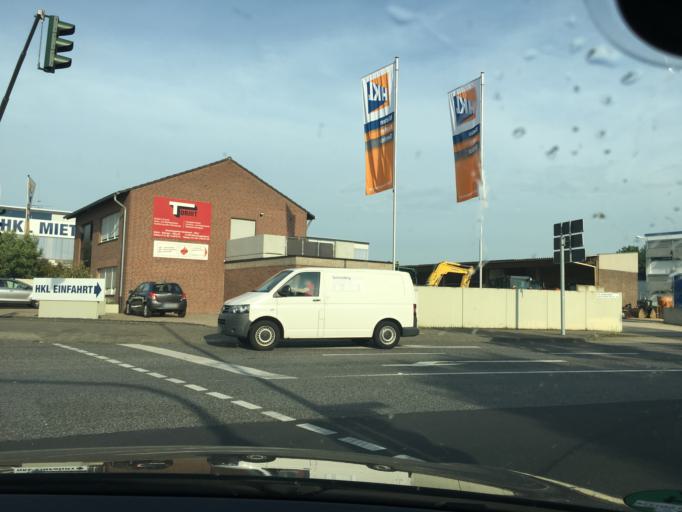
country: DE
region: North Rhine-Westphalia
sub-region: Regierungsbezirk Dusseldorf
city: Monchengladbach
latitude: 51.1400
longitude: 6.4131
